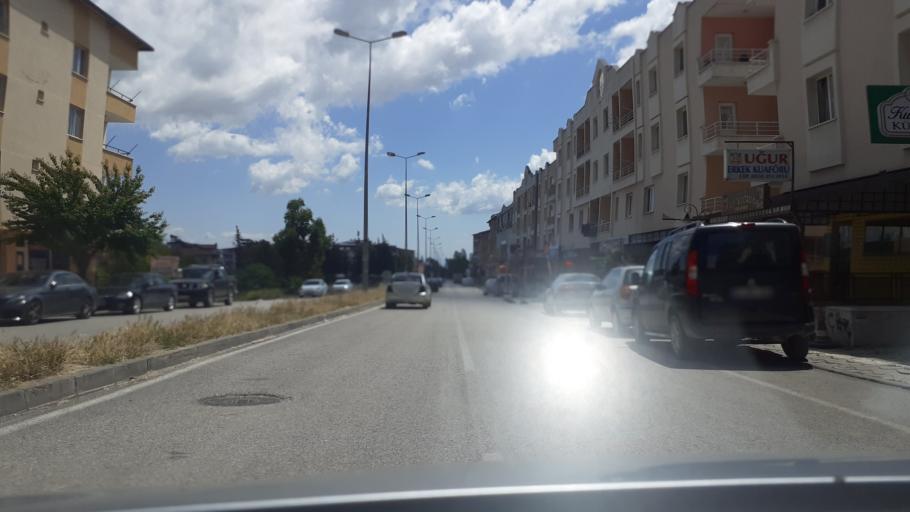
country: TR
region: Hatay
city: Anayazi
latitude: 36.3350
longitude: 36.2004
